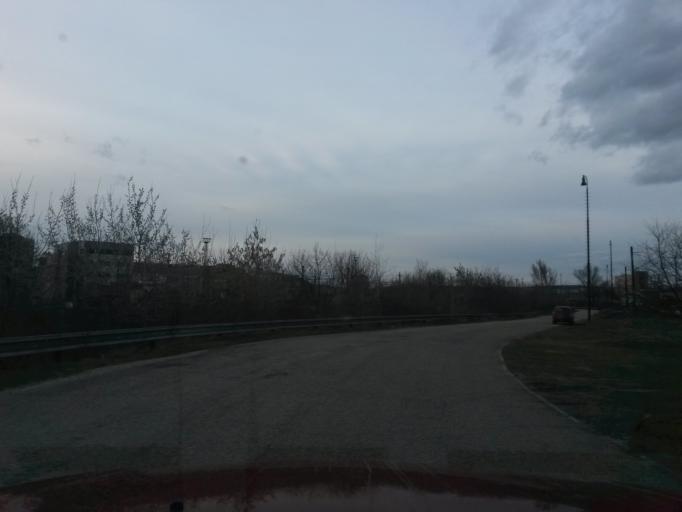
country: SK
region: Kosicky
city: Kosice
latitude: 48.7153
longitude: 21.2711
